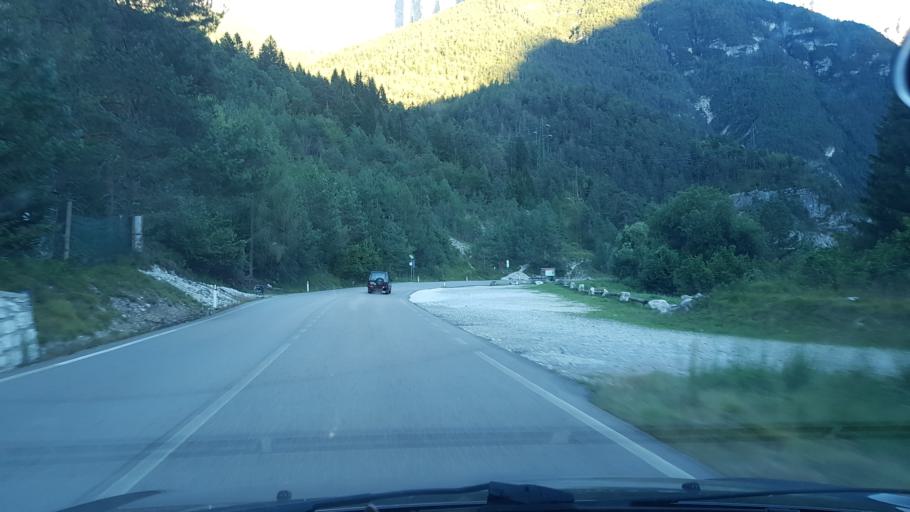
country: IT
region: Veneto
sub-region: Provincia di Belluno
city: Forno di Zoldo
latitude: 46.3398
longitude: 12.2227
